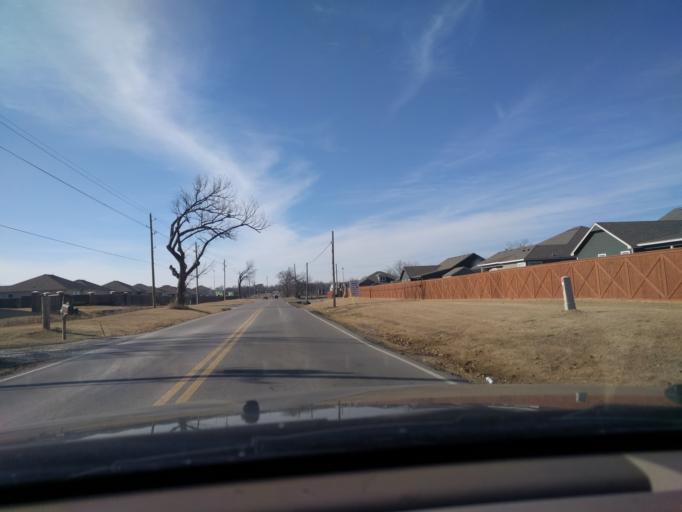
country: US
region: Oklahoma
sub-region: Wagoner County
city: Coweta
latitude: 36.0317
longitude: -95.6930
